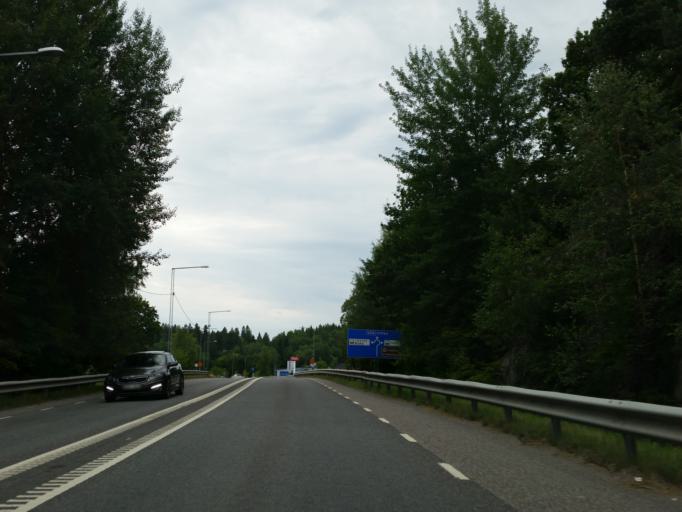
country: SE
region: Stockholm
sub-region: Botkyrka Kommun
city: Tumba
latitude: 59.2171
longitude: 17.8298
